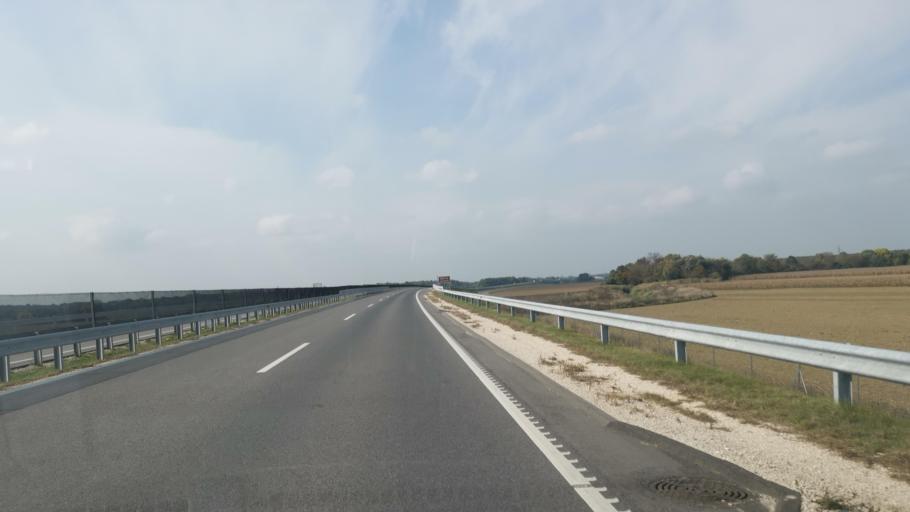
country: HU
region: Gyor-Moson-Sopron
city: Kapuvar
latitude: 47.5705
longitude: 17.0168
